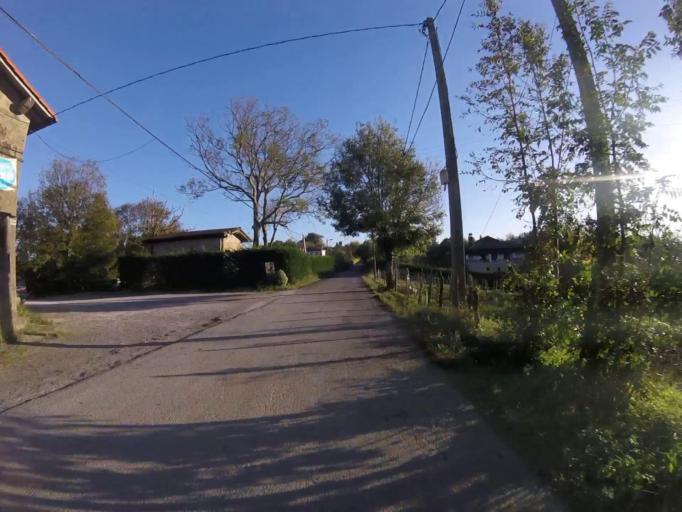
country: ES
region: Basque Country
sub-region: Provincia de Guipuzcoa
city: Lasarte
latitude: 43.2905
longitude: -2.0153
